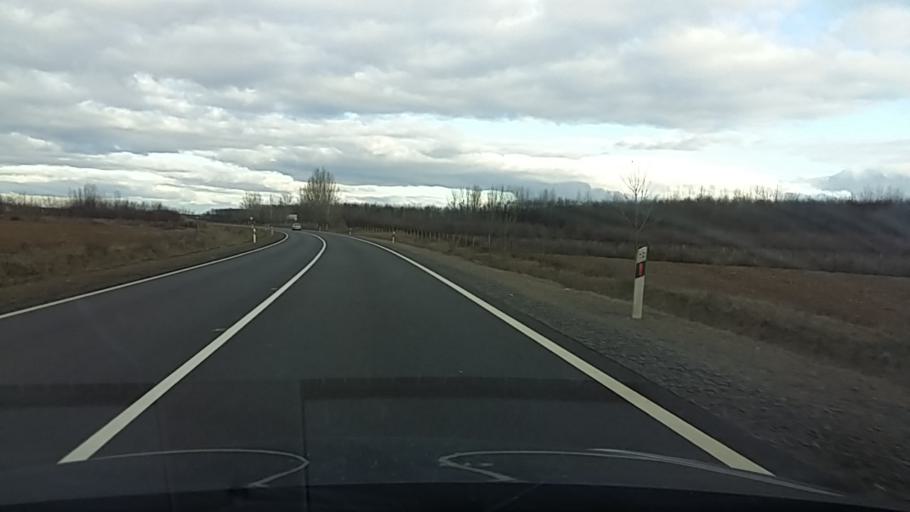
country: HU
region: Szabolcs-Szatmar-Bereg
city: Nyirpazony
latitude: 48.0049
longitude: 21.8421
